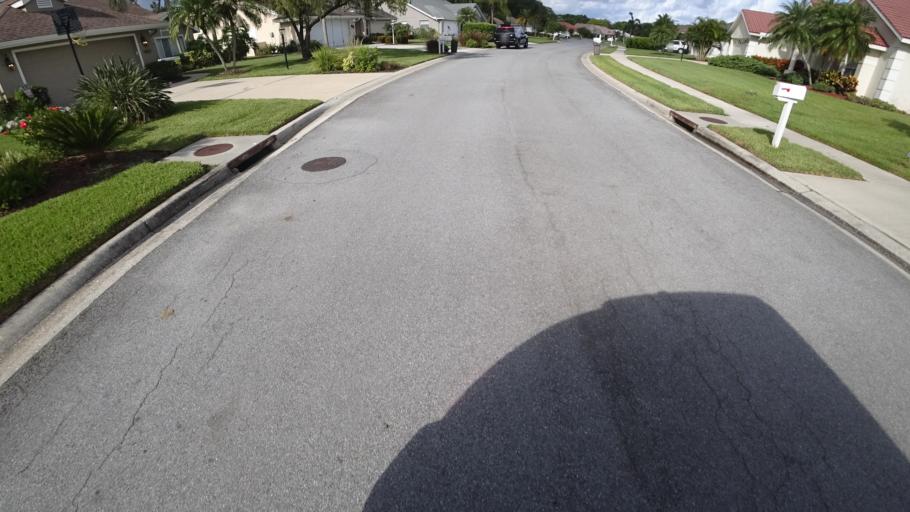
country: US
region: Florida
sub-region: Sarasota County
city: Desoto Lakes
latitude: 27.4164
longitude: -82.4859
